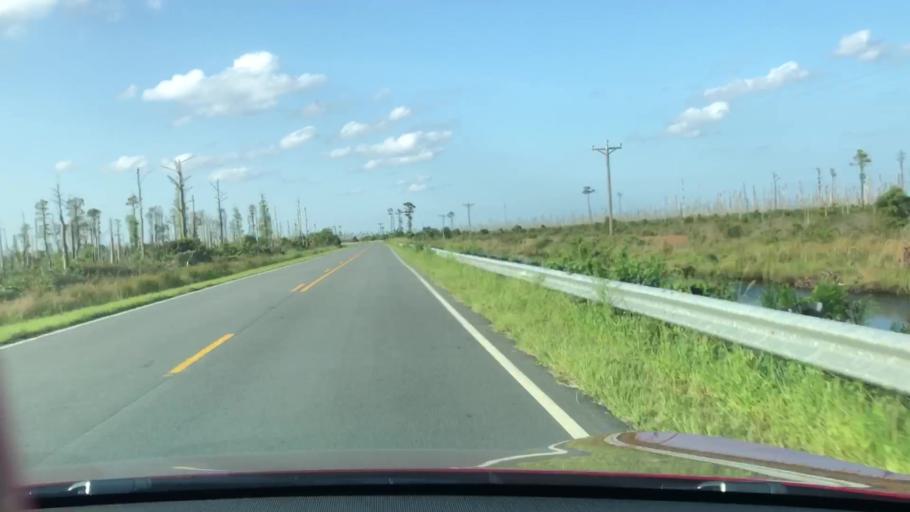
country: US
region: North Carolina
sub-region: Dare County
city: Wanchese
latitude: 35.6418
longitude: -75.7777
